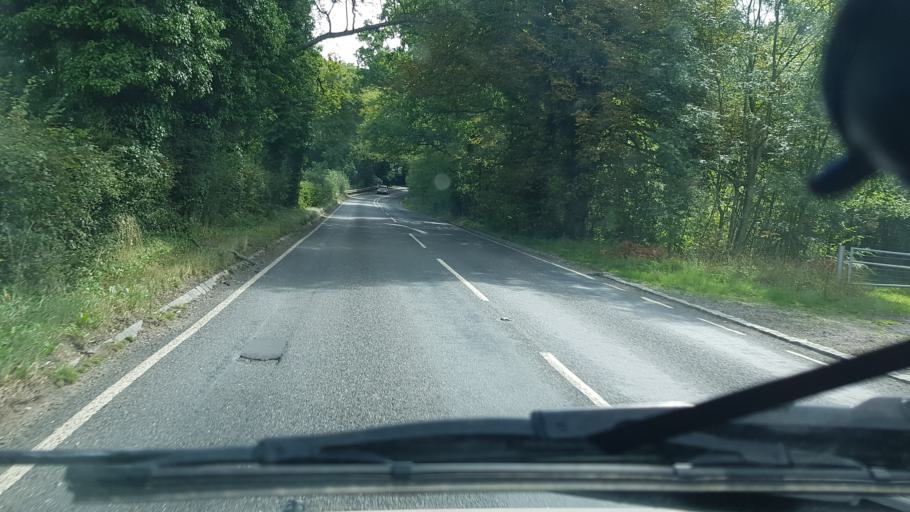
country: GB
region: England
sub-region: West Sussex
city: Rudgwick
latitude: 51.0956
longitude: -0.4797
